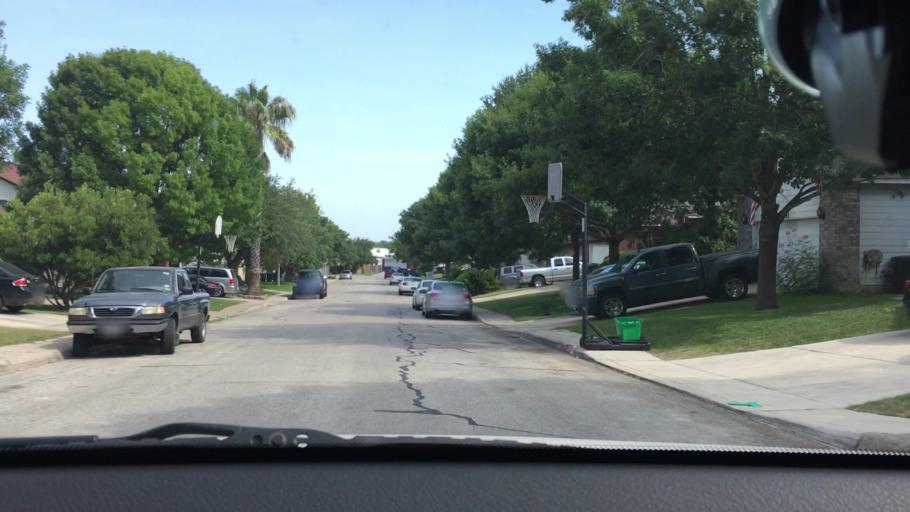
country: US
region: Texas
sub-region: Bexar County
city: Live Oak
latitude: 29.5811
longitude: -98.3754
